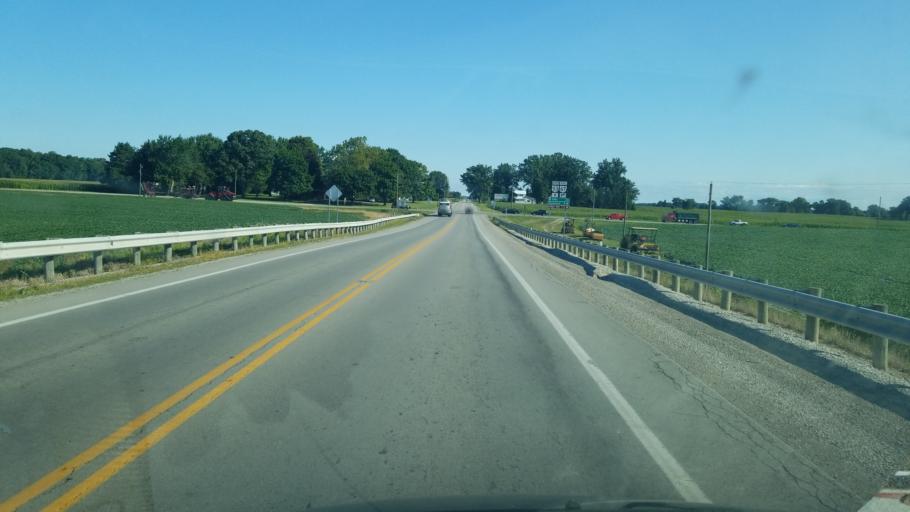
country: US
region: Ohio
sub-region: Wyandot County
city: Upper Sandusky
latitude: 40.8600
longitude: -83.2790
